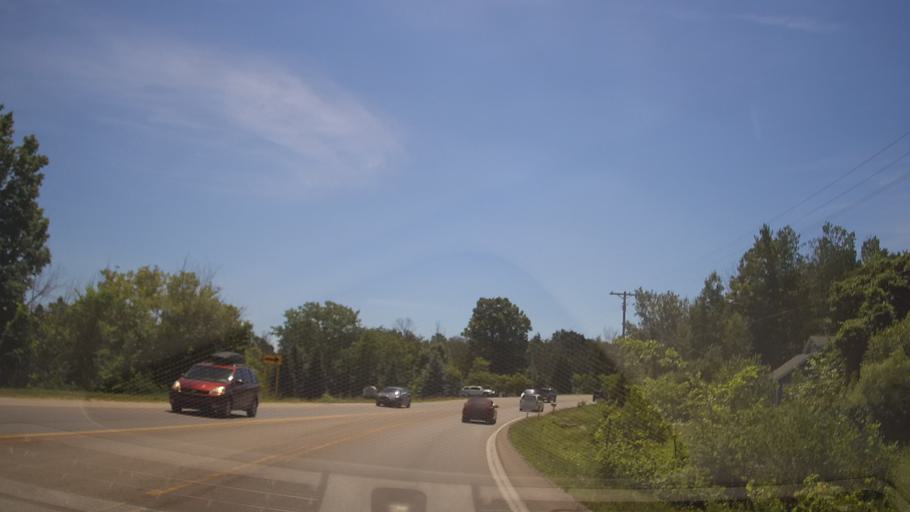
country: US
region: Michigan
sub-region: Grand Traverse County
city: Traverse City
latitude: 44.7350
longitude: -85.6561
